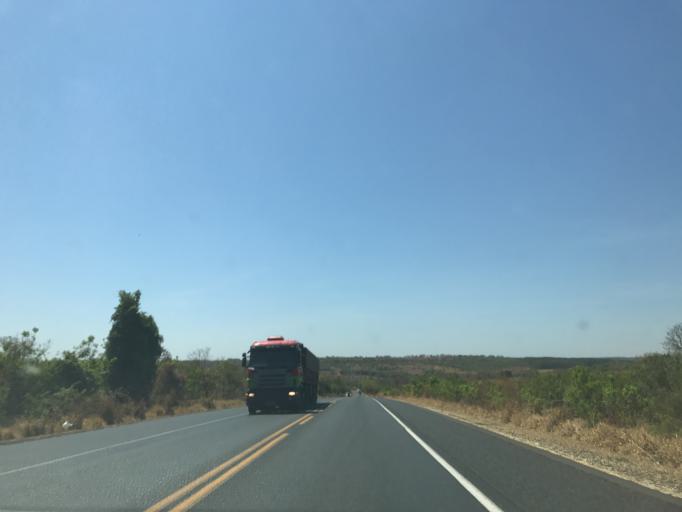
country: BR
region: Minas Gerais
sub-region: Prata
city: Prata
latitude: -19.3598
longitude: -48.9000
